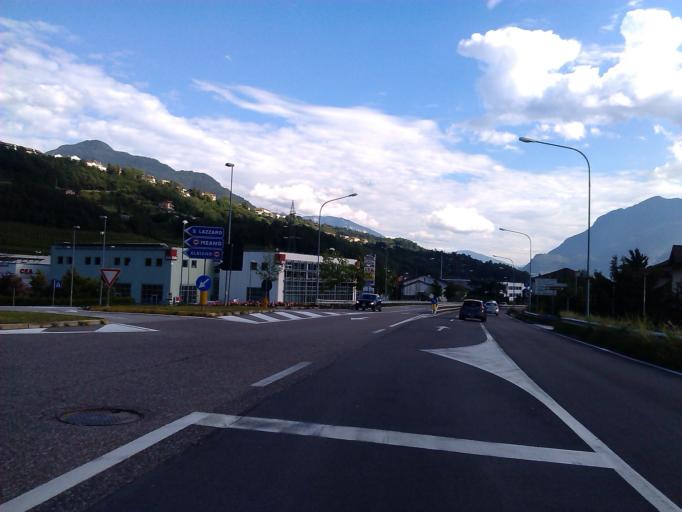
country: IT
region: Trentino-Alto Adige
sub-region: Provincia di Trento
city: Lavis
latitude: 46.1342
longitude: 11.1110
